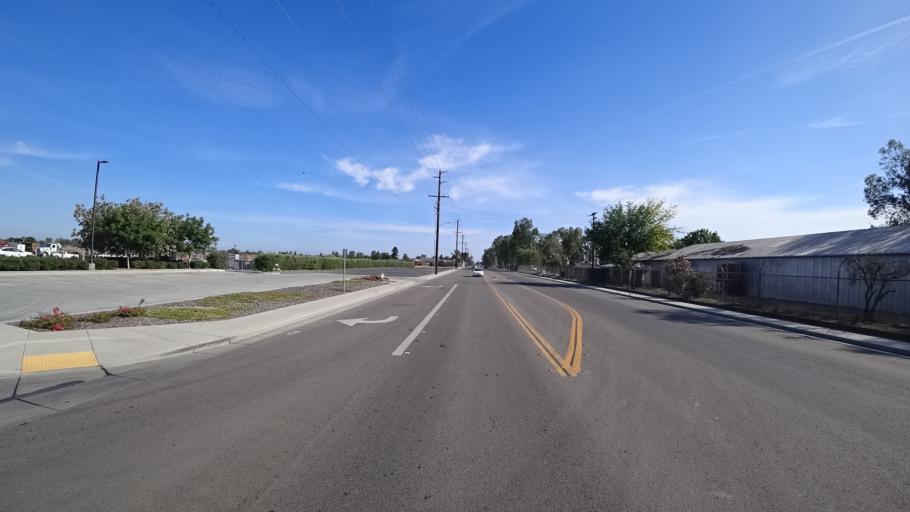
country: US
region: California
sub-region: Kings County
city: Home Garden
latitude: 36.3157
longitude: -119.6371
